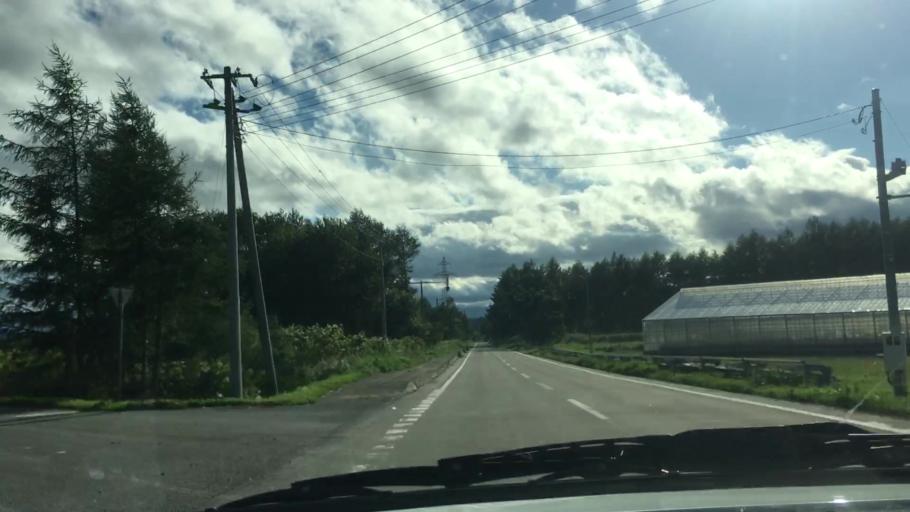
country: JP
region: Hokkaido
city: Otofuke
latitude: 43.1827
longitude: 143.0163
